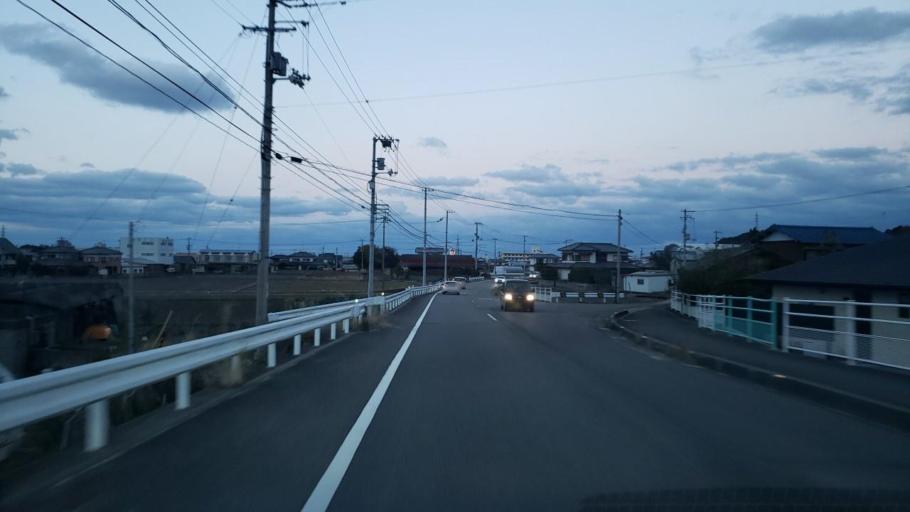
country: JP
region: Tokushima
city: Kamojimacho-jogejima
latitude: 34.2351
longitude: 134.3474
